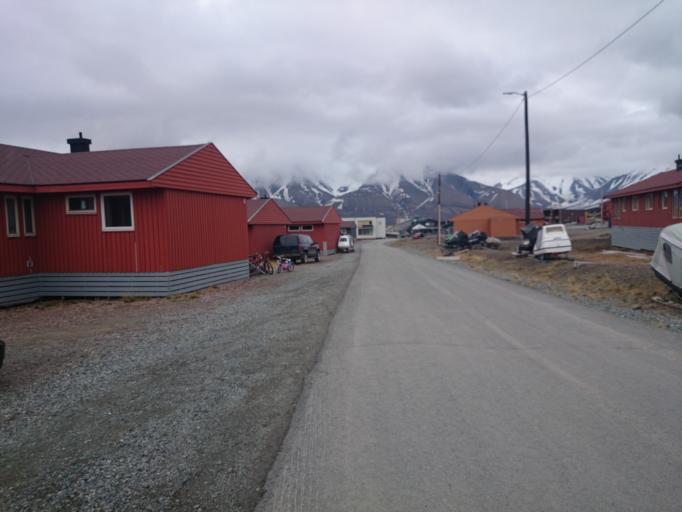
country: SJ
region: Svalbard
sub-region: Spitsbergen
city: Longyearbyen
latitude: 78.2157
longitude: 15.6286
